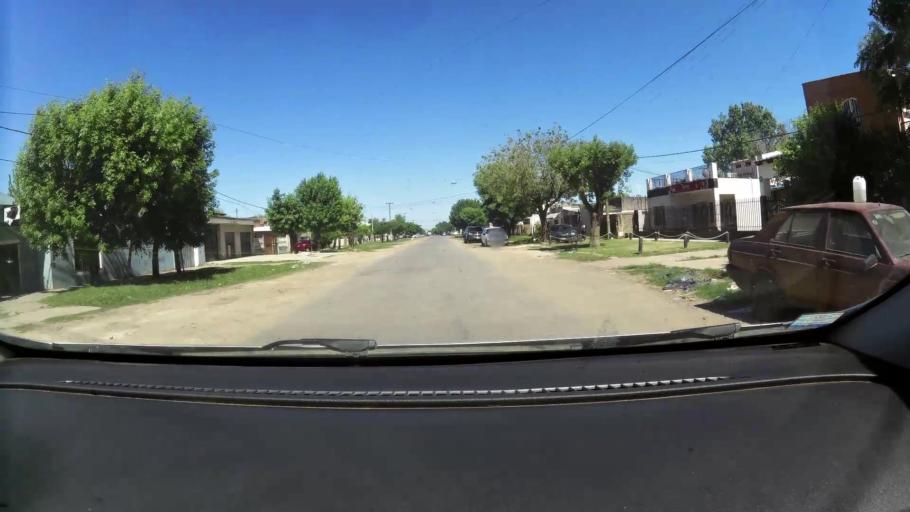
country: AR
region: Santa Fe
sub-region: Departamento de Rosario
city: Rosario
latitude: -32.9744
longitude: -60.6933
